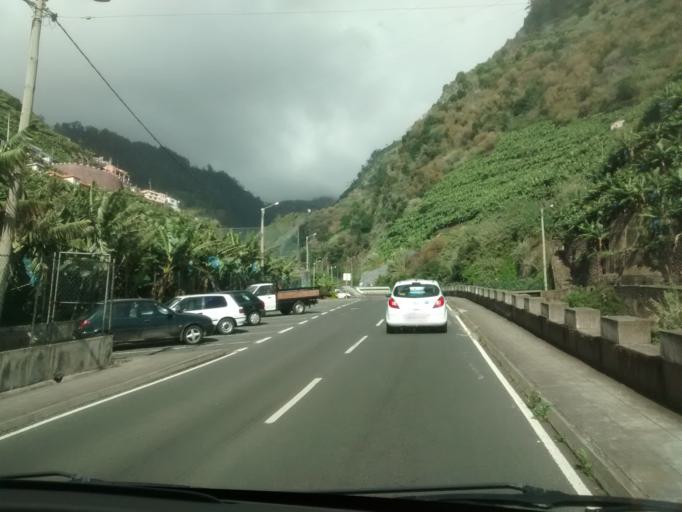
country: PT
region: Madeira
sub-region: Calheta
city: Arco da Calheta
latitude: 32.7034
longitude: -17.1347
